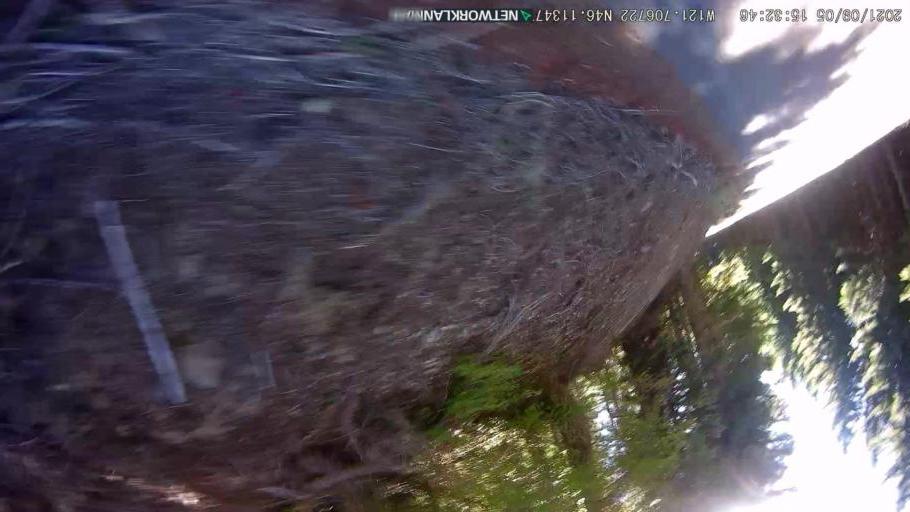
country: US
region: Washington
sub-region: Skamania County
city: Carson
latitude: 46.1132
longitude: -121.7067
